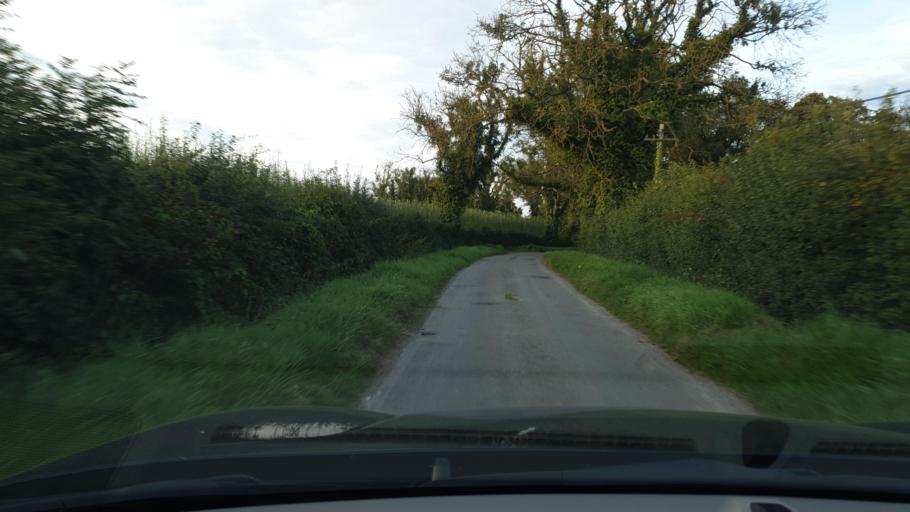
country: IE
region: Leinster
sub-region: An Mhi
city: Ashbourne
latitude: 53.5346
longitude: -6.3579
